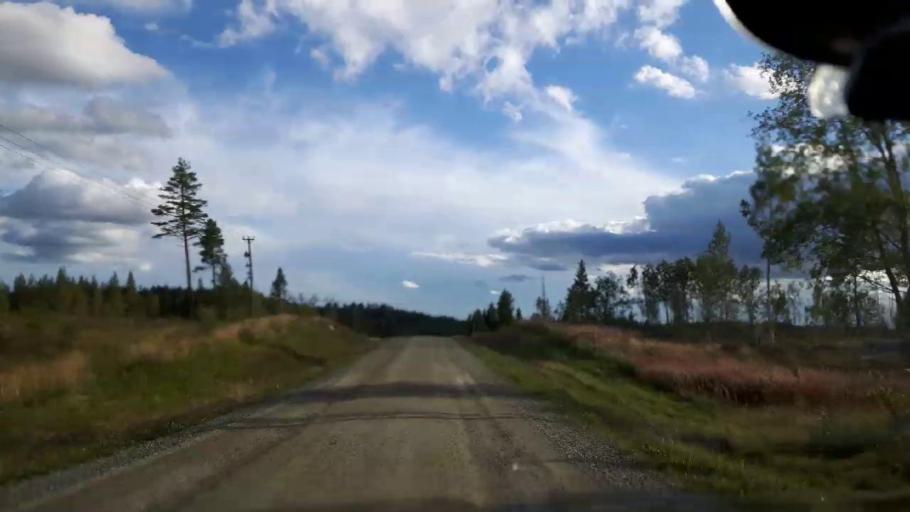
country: SE
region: Jaemtland
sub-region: Stroemsunds Kommun
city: Stroemsund
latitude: 63.3077
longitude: 15.6006
